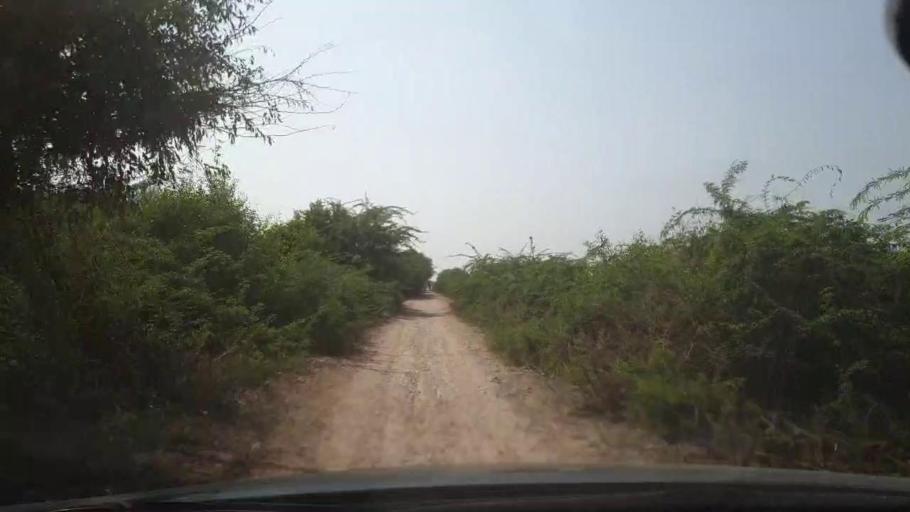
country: PK
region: Sindh
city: Naukot
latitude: 24.7959
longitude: 69.2424
